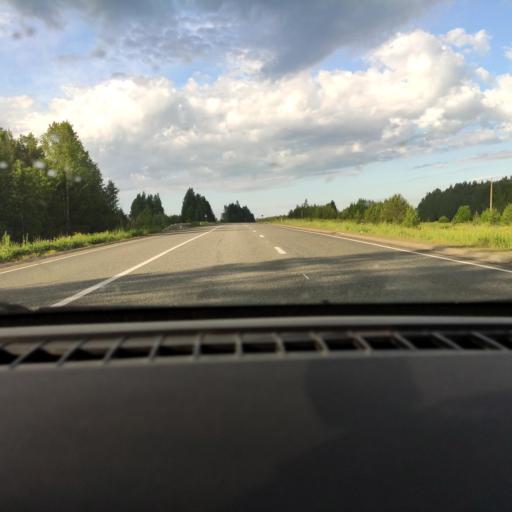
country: RU
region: Udmurtiya
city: Votkinsk
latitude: 57.2519
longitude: 54.2216
